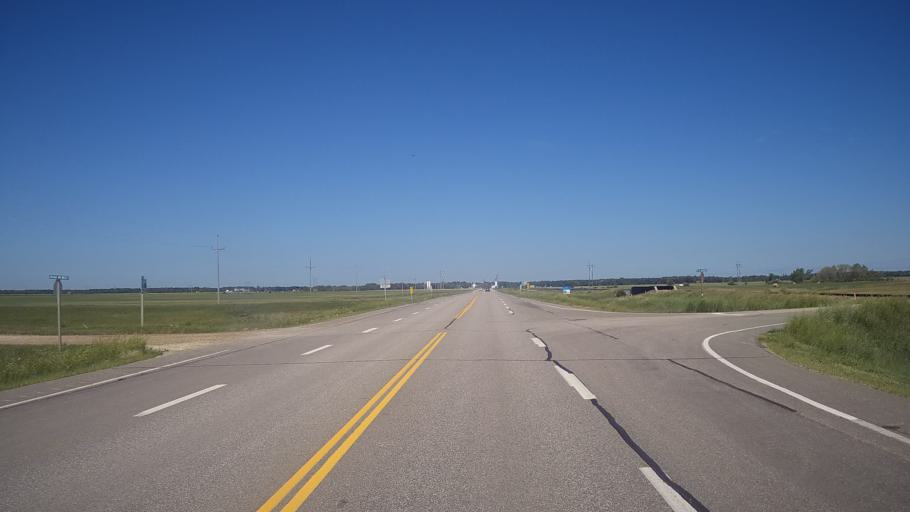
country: CA
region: Manitoba
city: Portage la Prairie
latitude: 50.1181
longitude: -98.5591
